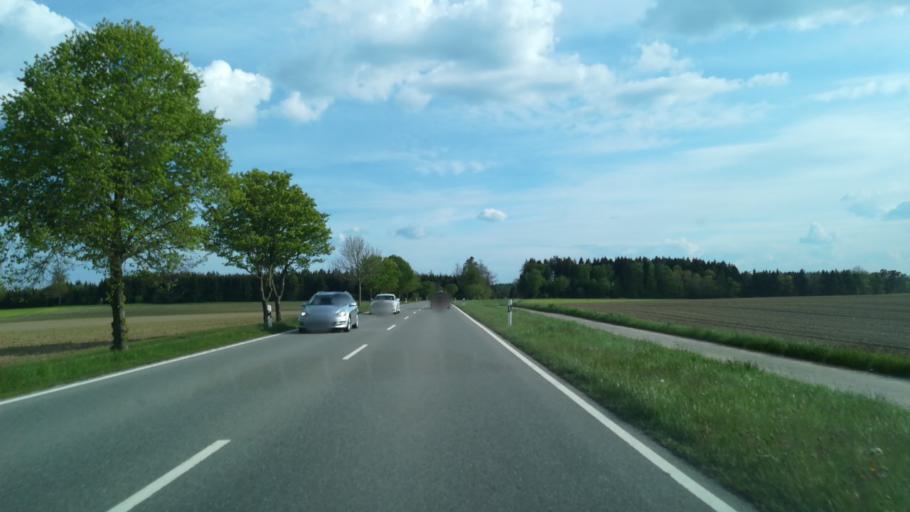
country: DE
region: Baden-Wuerttemberg
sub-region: Freiburg Region
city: Muhlingen
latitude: 47.9502
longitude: 9.0447
